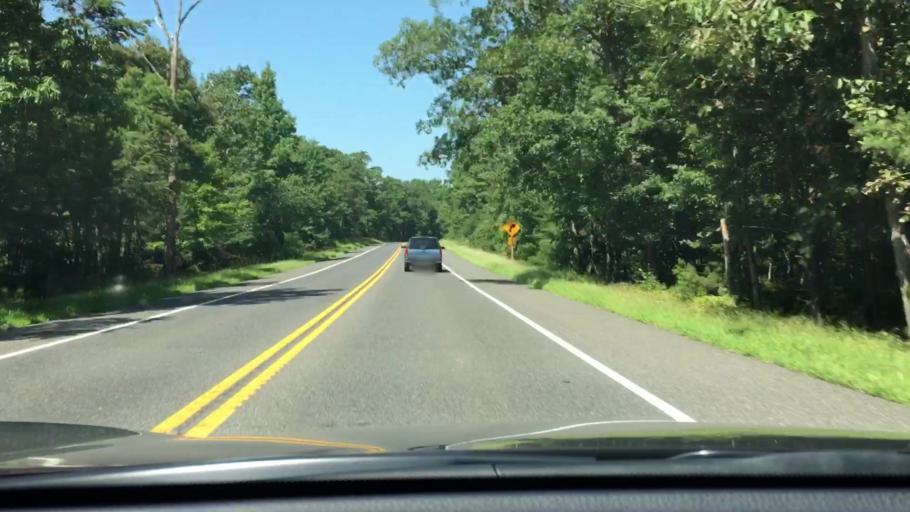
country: US
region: New Jersey
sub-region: Cumberland County
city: Port Norris
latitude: 39.2855
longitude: -74.9548
